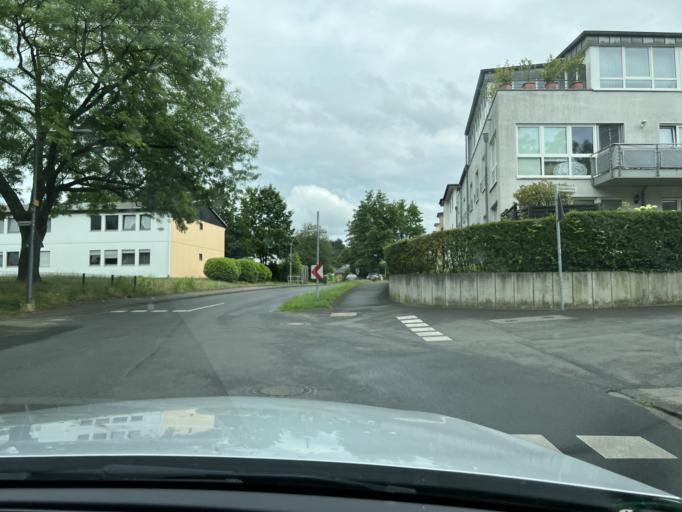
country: DE
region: North Rhine-Westphalia
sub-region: Regierungsbezirk Koln
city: Merheim
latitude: 50.9691
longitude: 7.0703
